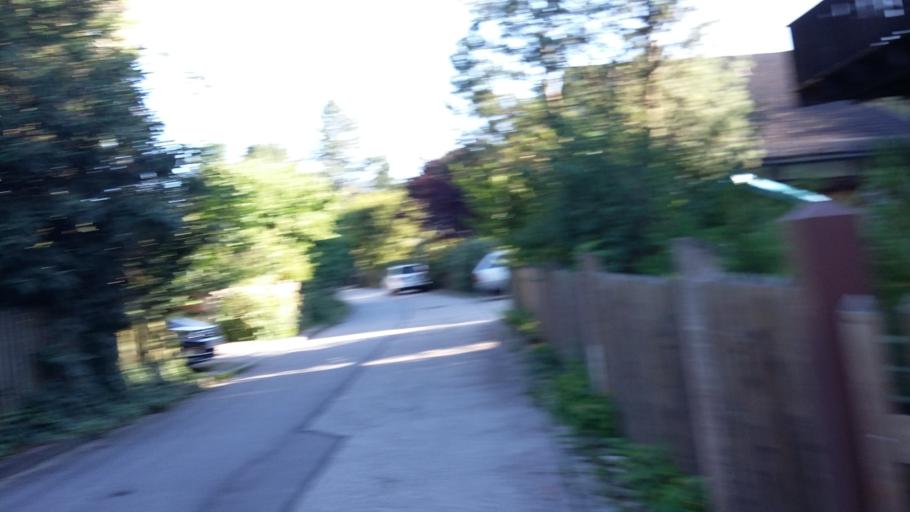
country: DE
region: Bavaria
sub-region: Upper Bavaria
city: Gauting
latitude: 48.0654
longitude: 11.3724
